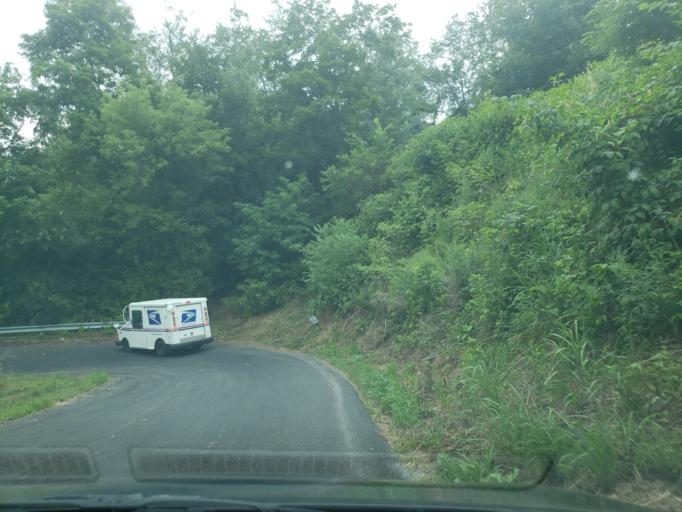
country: US
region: Pennsylvania
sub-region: Allegheny County
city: Ben Avon
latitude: 40.5115
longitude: -80.0782
